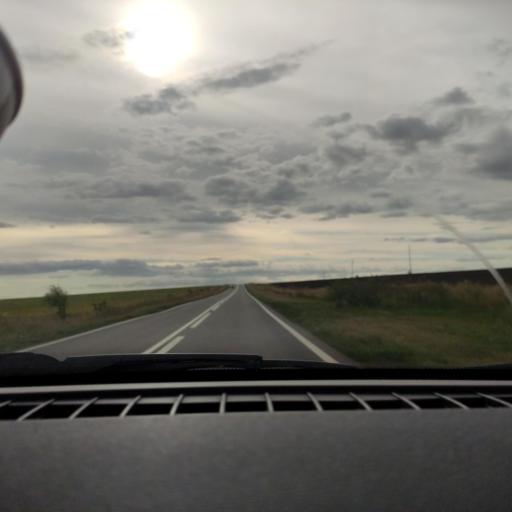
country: RU
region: Samara
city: Georgiyevka
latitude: 53.4170
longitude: 50.9038
